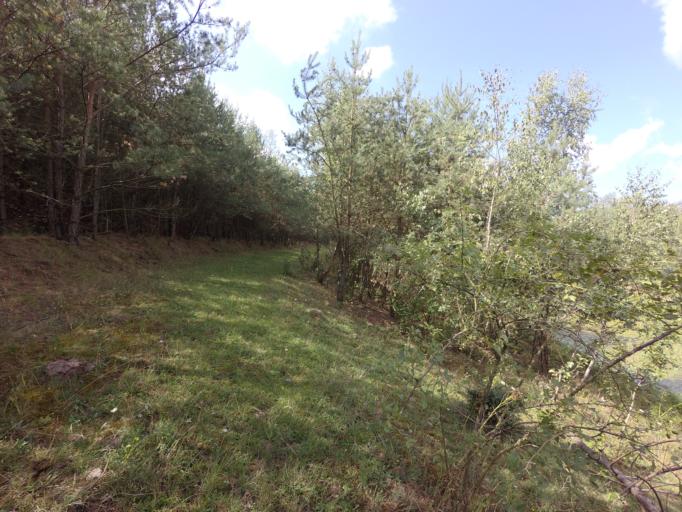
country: NL
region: Limburg
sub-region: Gemeente Brunssum
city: Brunssum
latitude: 50.9296
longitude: 6.0301
